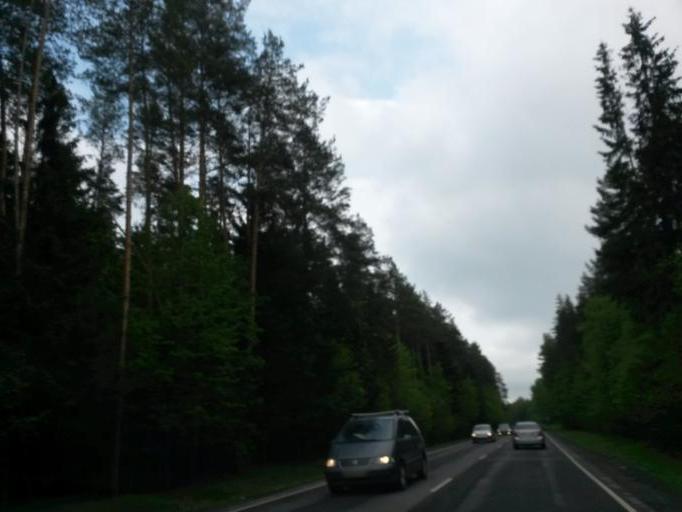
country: RU
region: Moskovskaya
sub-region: Podol'skiy Rayon
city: Podol'sk
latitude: 55.3805
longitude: 37.6336
